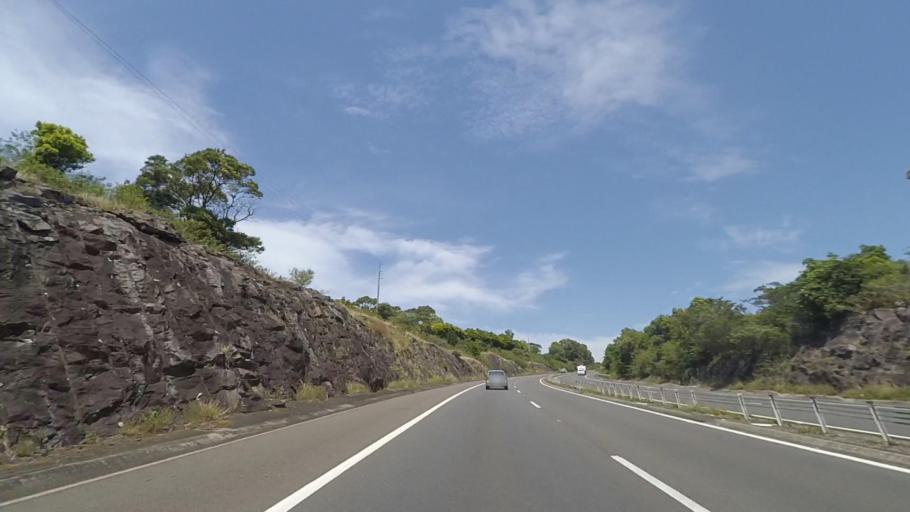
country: AU
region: New South Wales
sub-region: Kiama
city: Kiama
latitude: -34.6924
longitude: 150.8443
